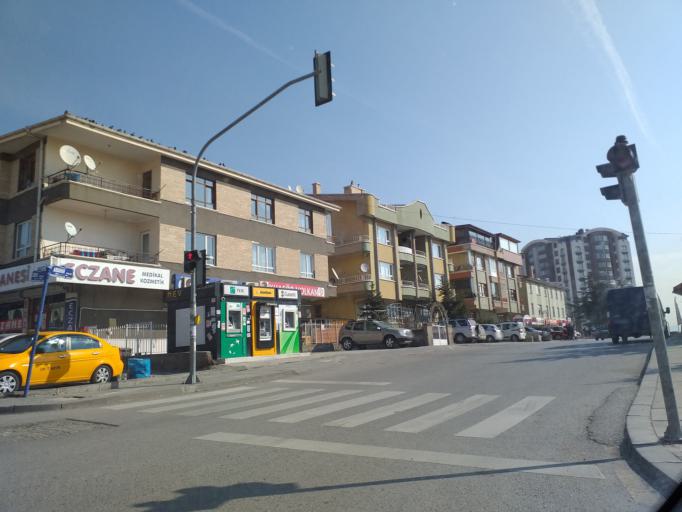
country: TR
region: Ankara
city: Mamak
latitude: 40.0037
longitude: 32.8560
